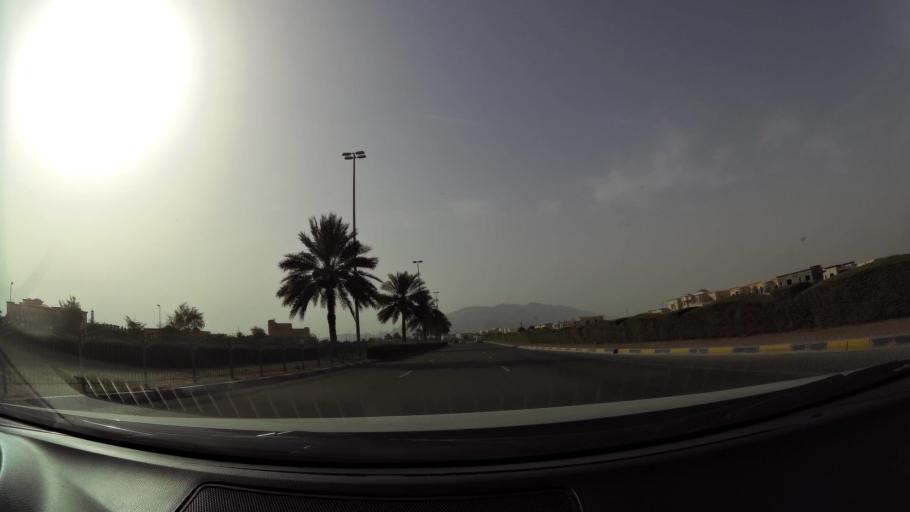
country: AE
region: Abu Dhabi
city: Al Ain
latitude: 24.1332
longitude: 55.7026
